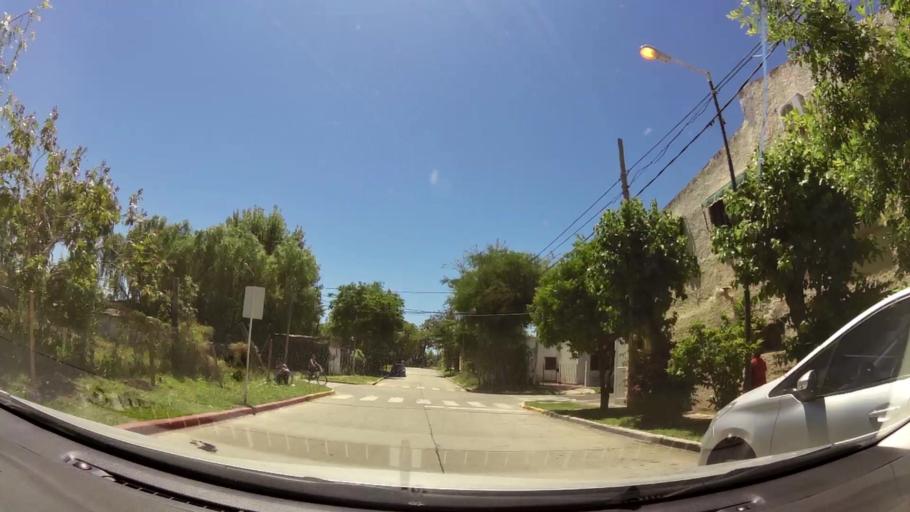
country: AR
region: Buenos Aires
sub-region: Partido de Tigre
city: Tigre
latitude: -34.4548
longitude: -58.5516
